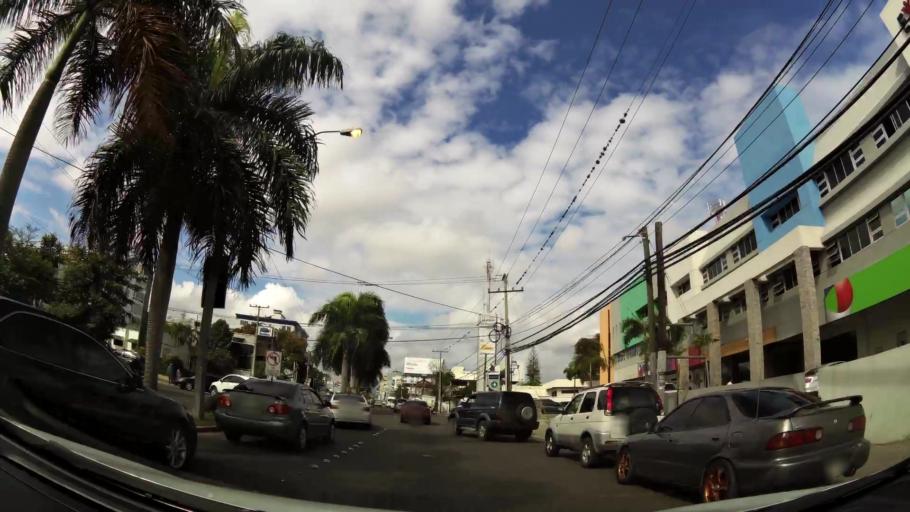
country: DO
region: Santiago
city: Santiago de los Caballeros
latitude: 19.4609
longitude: -70.6893
